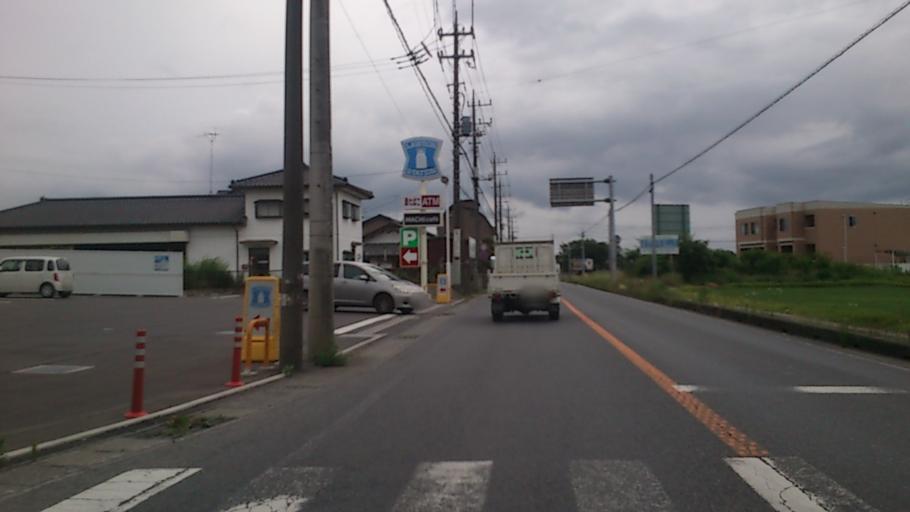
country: JP
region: Ibaraki
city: Ishige
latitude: 36.1053
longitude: 140.0481
